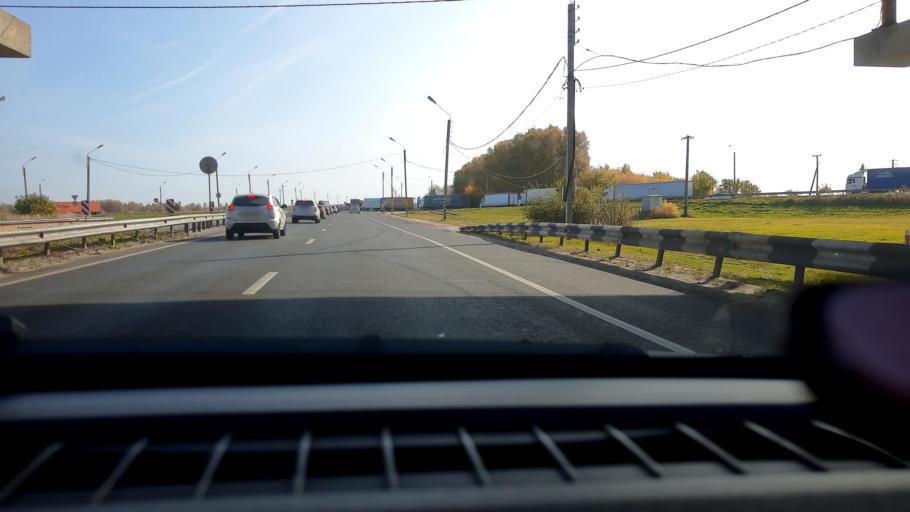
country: RU
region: Nizjnij Novgorod
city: Kstovo
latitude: 56.1274
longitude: 44.2606
